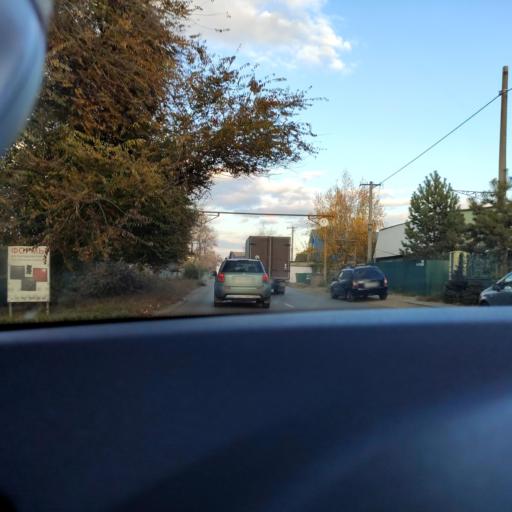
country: RU
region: Samara
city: Smyshlyayevka
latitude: 53.2387
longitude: 50.3289
